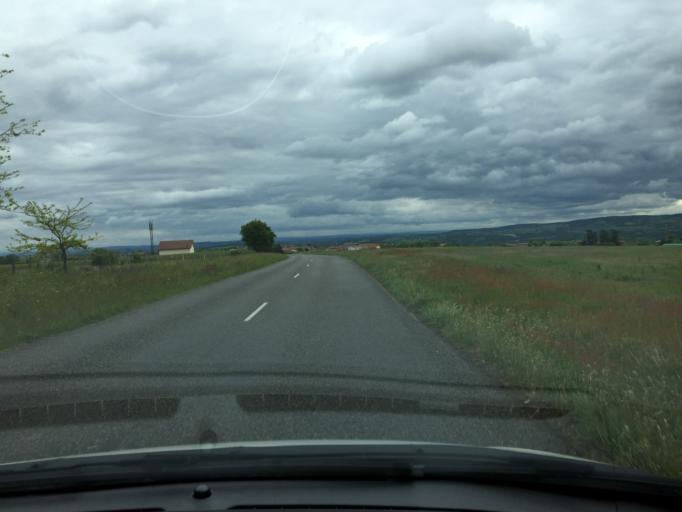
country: FR
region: Rhone-Alpes
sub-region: Departement du Rhone
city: Saint-Maurice-sur-Dargoire
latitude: 45.5895
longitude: 4.6573
